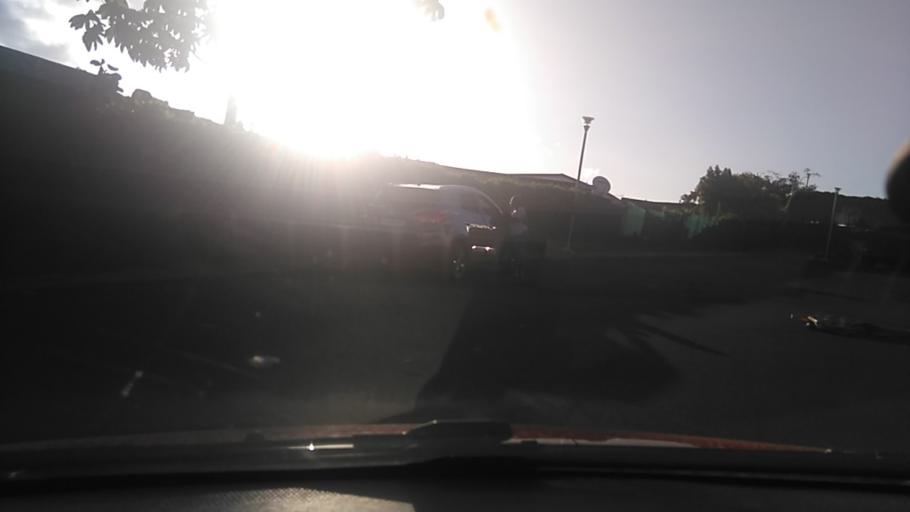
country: MQ
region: Martinique
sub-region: Martinique
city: Fort-de-France
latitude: 14.6033
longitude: -61.0928
